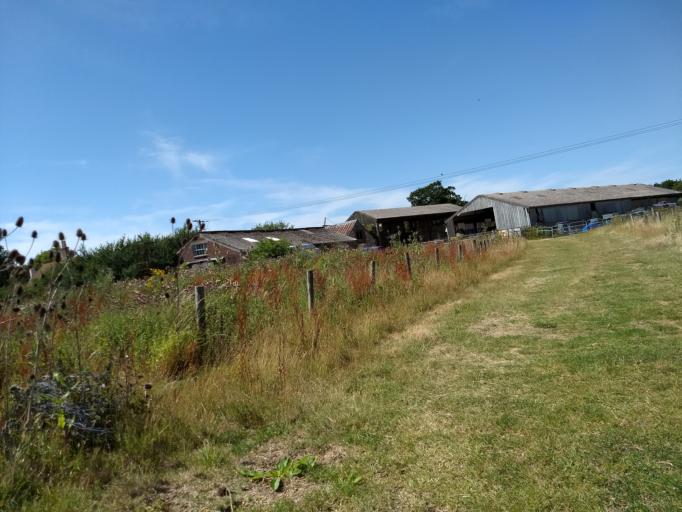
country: GB
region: England
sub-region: Isle of Wight
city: Ryde
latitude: 50.7027
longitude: -1.1609
